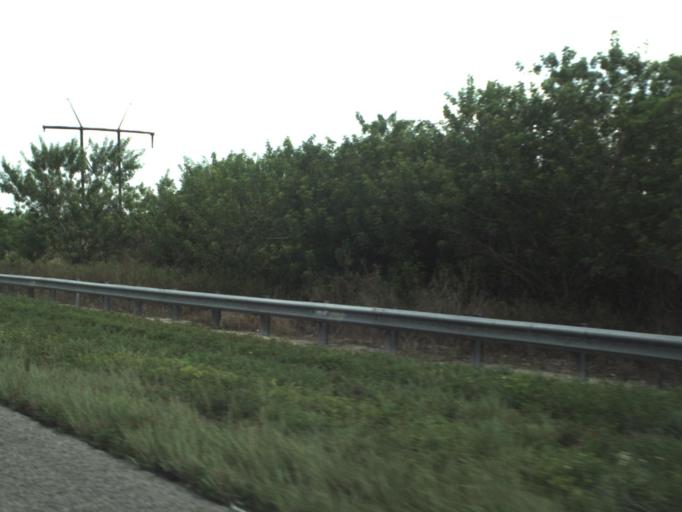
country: US
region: Florida
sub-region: Broward County
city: Weston
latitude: 26.2322
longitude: -80.4608
